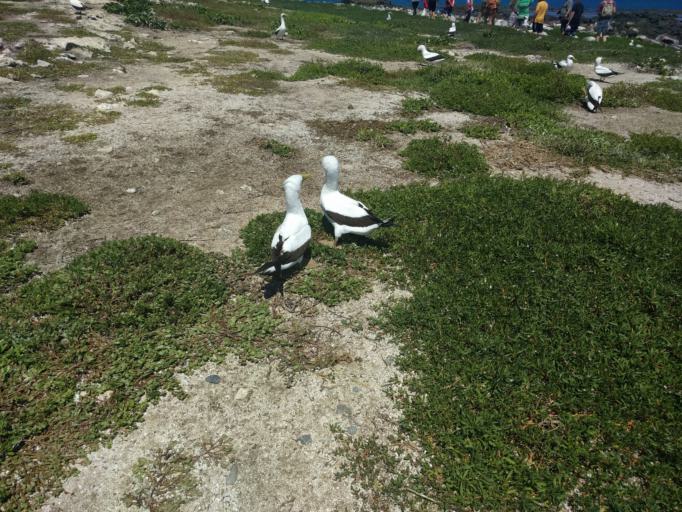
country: BR
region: Bahia
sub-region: Nova Vicosa
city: Nova Vicosa
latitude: -17.9702
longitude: -38.7107
